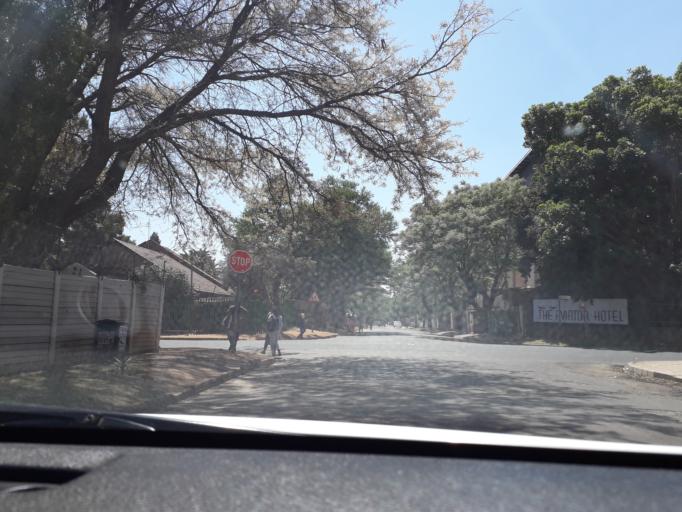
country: ZA
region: Gauteng
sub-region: City of Johannesburg Metropolitan Municipality
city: Modderfontein
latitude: -26.1059
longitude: 28.2408
